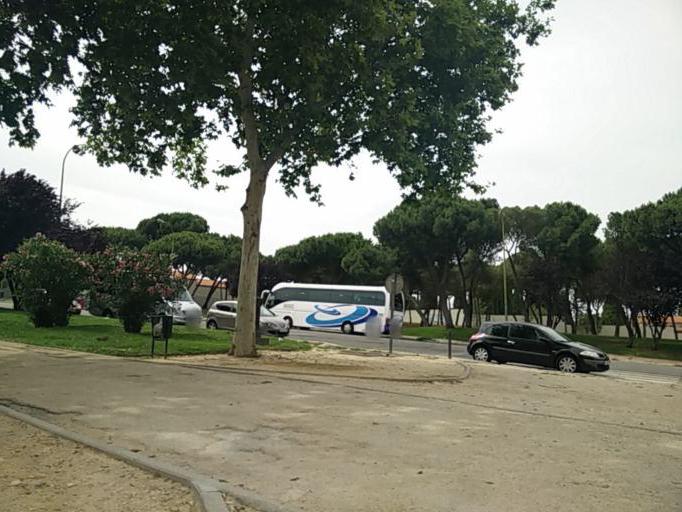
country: ES
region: Madrid
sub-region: Provincia de Madrid
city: Carabanchel
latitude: 40.3989
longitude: -3.7286
